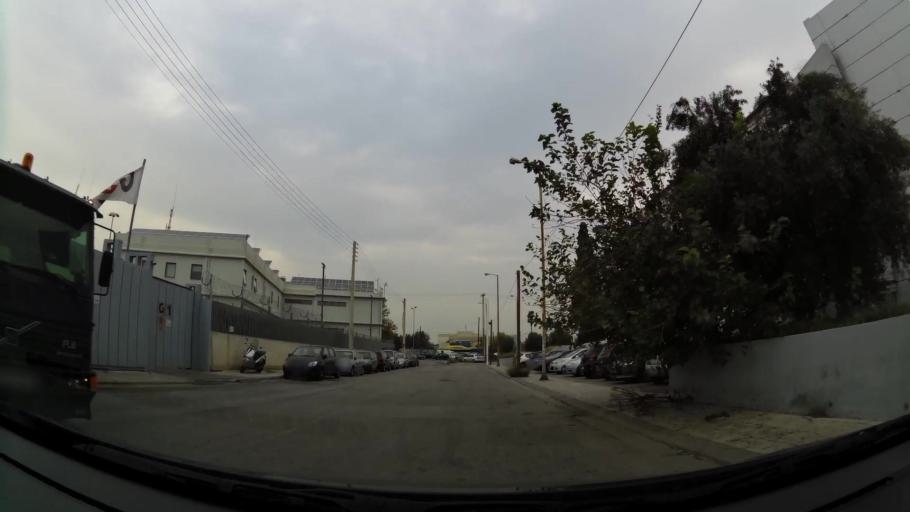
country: GR
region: Attica
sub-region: Nomos Piraios
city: Agios Ioannis Rentis
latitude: 37.9753
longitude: 23.6714
